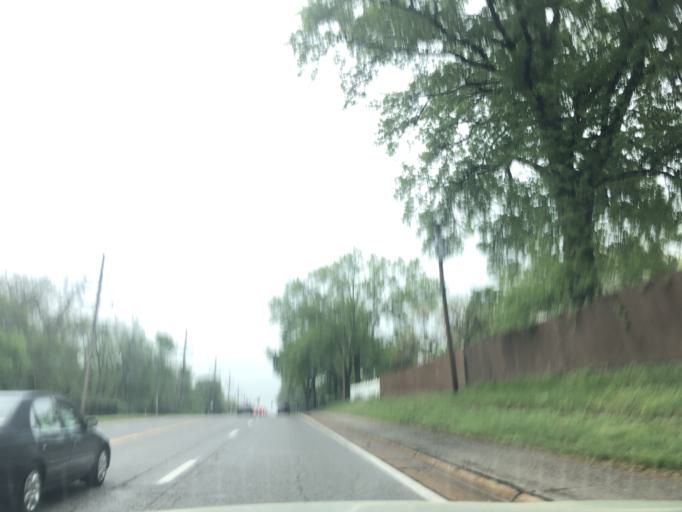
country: US
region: Missouri
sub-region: Saint Louis County
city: Marlborough
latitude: 38.5714
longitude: -90.3197
